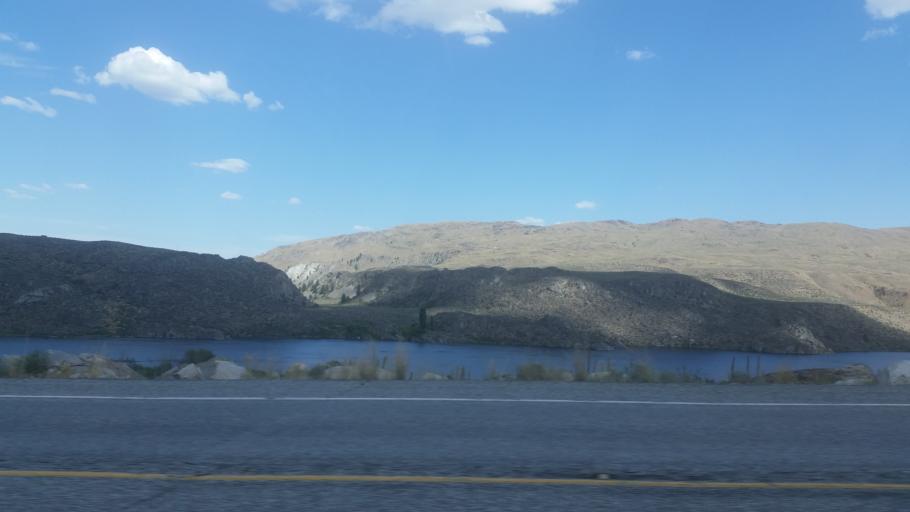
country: US
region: Washington
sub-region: Okanogan County
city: Brewster
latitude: 48.0347
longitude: -119.8946
